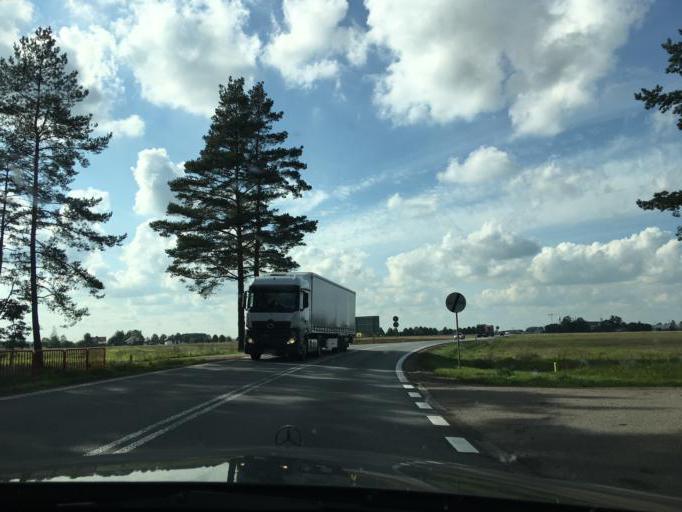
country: PL
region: Podlasie
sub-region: Suwalki
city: Suwalki
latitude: 54.0405
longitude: 22.9354
